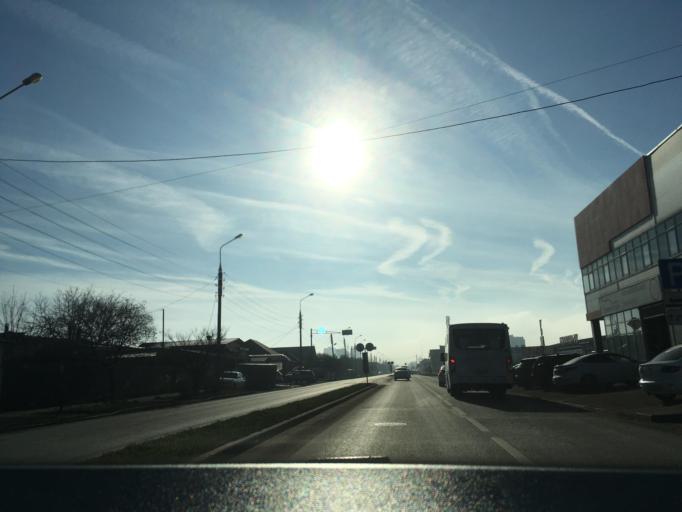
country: RU
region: Krasnodarskiy
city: Krasnodar
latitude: 45.1189
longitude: 39.0115
